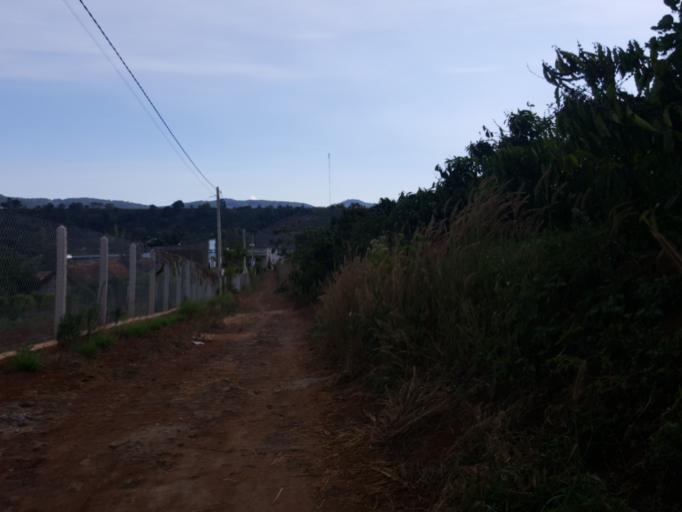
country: VN
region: Lam Dong
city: Duc Trong
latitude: 11.8373
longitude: 108.3485
